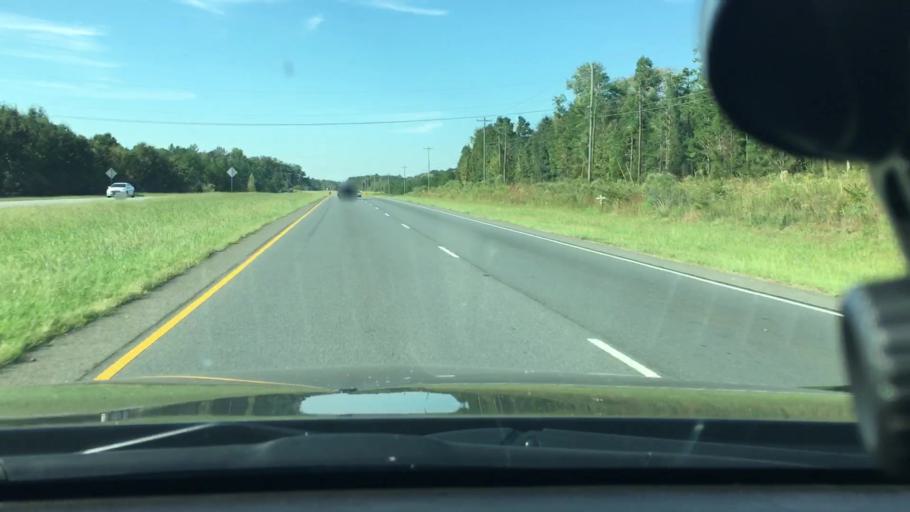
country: US
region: North Carolina
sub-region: Mecklenburg County
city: Mint Hill
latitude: 35.2445
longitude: -80.5878
